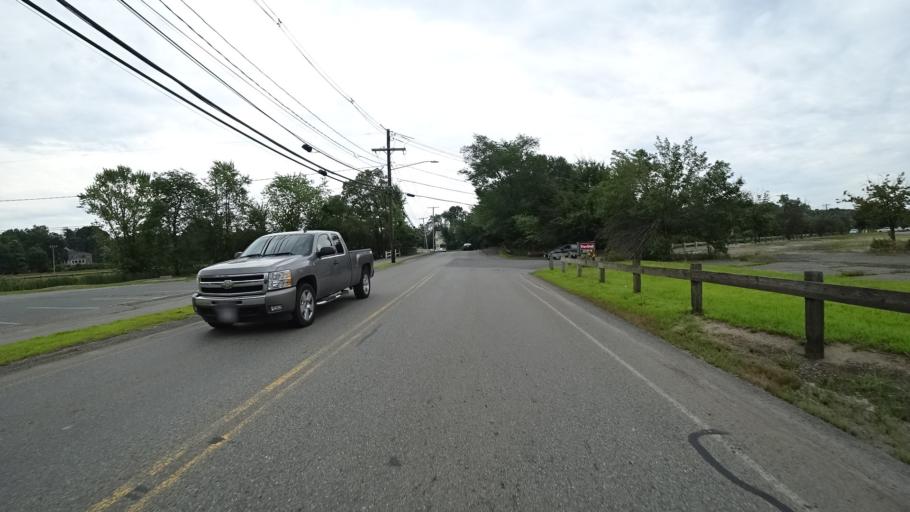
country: US
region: Massachusetts
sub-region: Norfolk County
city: Dedham
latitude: 42.2448
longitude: -71.1712
